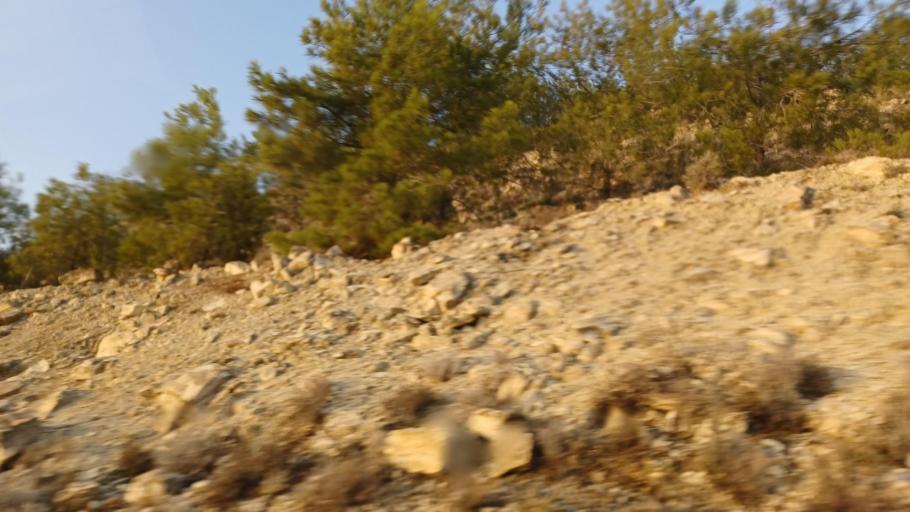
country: CY
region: Lefkosia
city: Lympia
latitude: 34.9969
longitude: 33.5245
